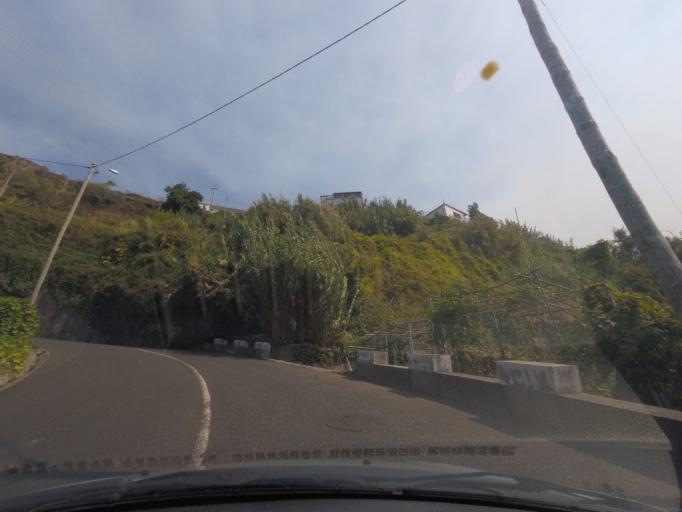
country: PT
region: Madeira
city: Ribeira Brava
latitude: 32.6828
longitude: -17.0708
